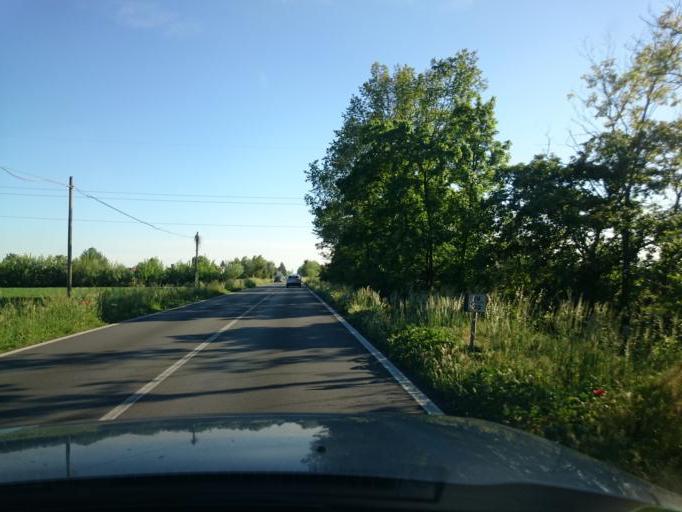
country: IT
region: Veneto
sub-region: Provincia di Venezia
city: Caselle
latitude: 45.4756
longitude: 12.0003
